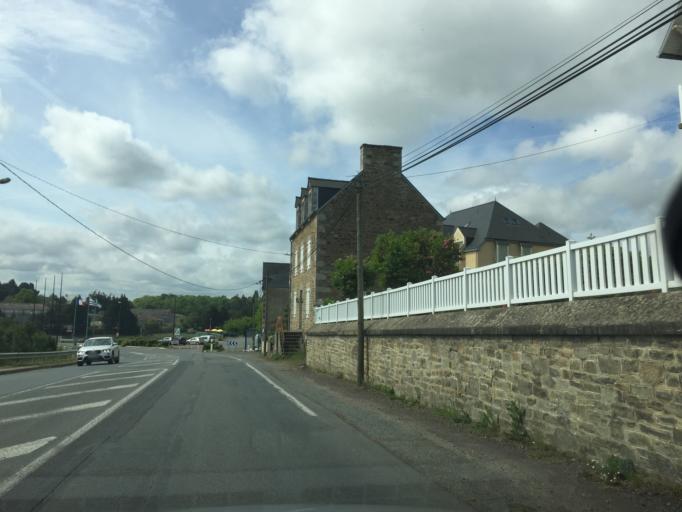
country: FR
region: Brittany
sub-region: Departement des Cotes-d'Armor
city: Crehen
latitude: 48.5755
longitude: -2.2143
